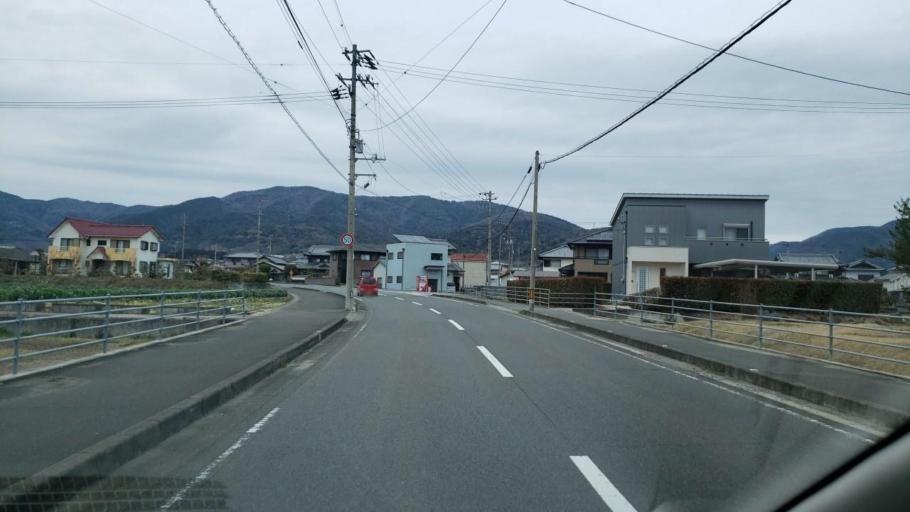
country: JP
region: Tokushima
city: Kamojimacho-jogejima
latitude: 34.1070
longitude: 134.3413
